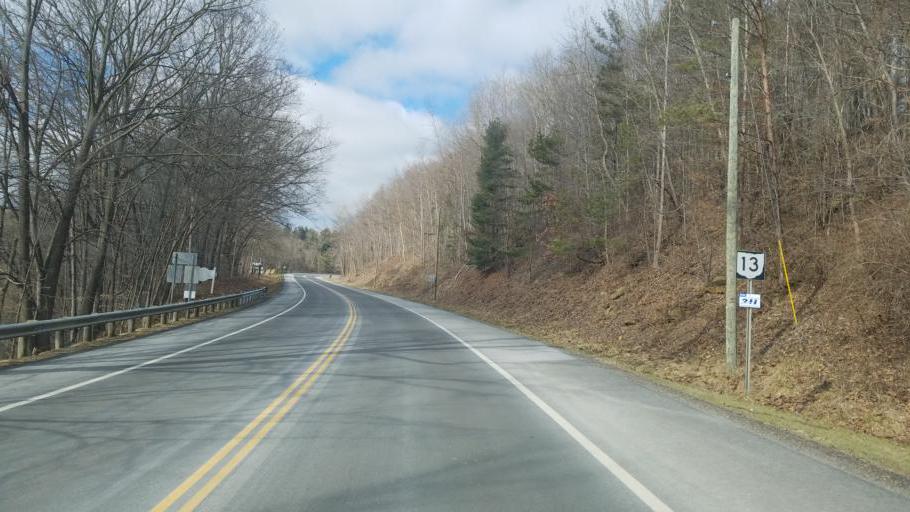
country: US
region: Ohio
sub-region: Sandusky County
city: Bellville
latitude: 40.6262
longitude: -82.5144
